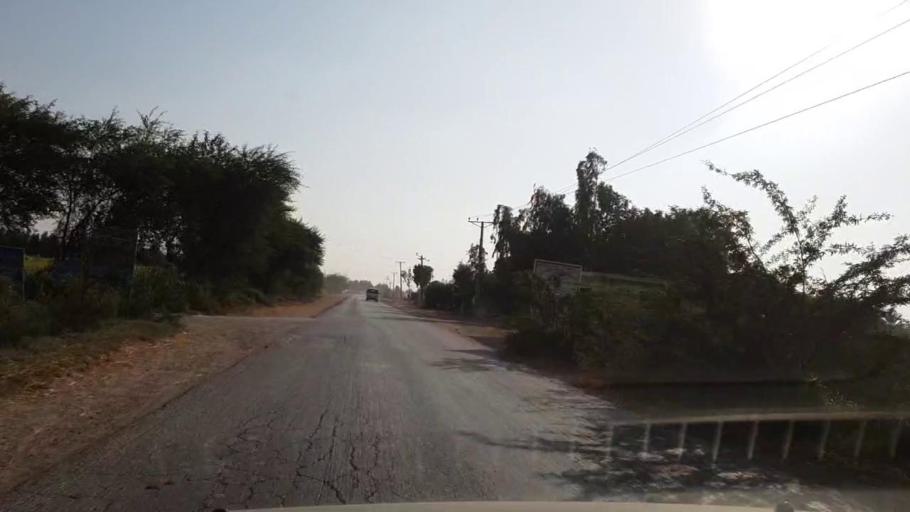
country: PK
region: Sindh
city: Bulri
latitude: 24.8686
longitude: 68.3383
